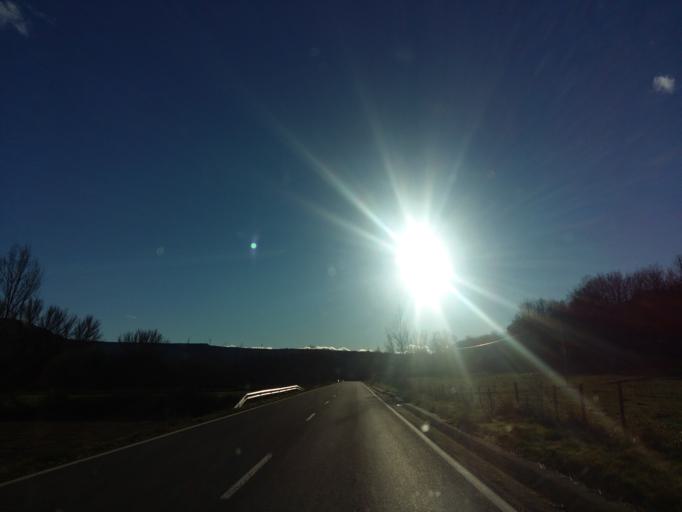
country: ES
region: Cantabria
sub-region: Provincia de Cantabria
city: San Martin de Elines
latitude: 42.8267
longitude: -3.9057
